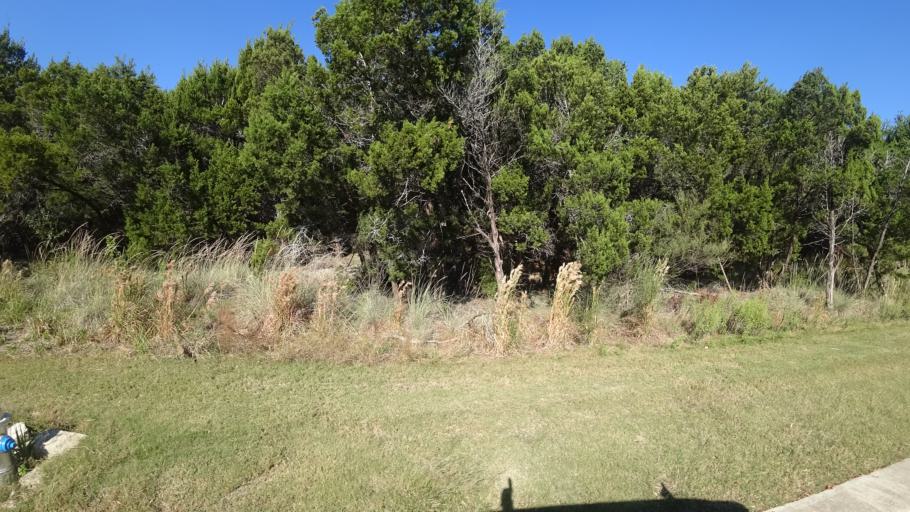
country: US
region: Texas
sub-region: Travis County
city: Barton Creek
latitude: 30.3517
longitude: -97.8867
